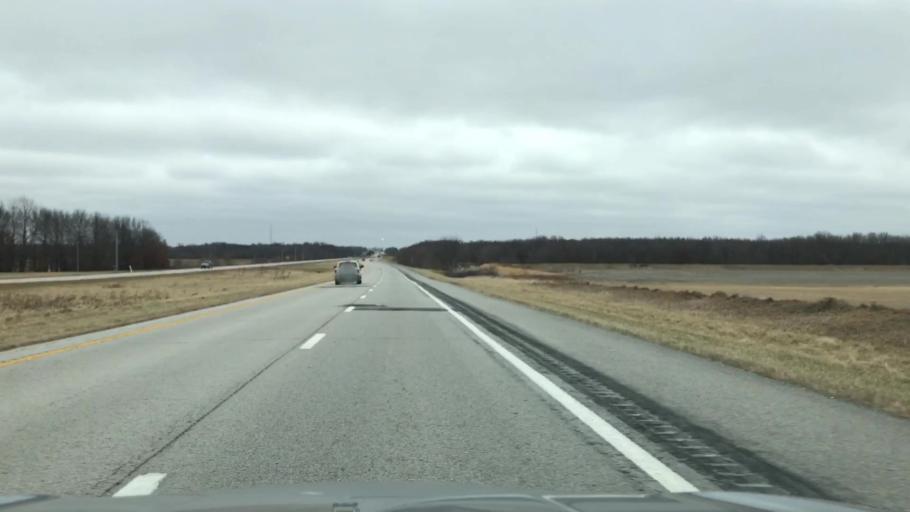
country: US
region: Missouri
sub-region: Linn County
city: Linneus
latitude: 39.7773
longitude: -93.3376
